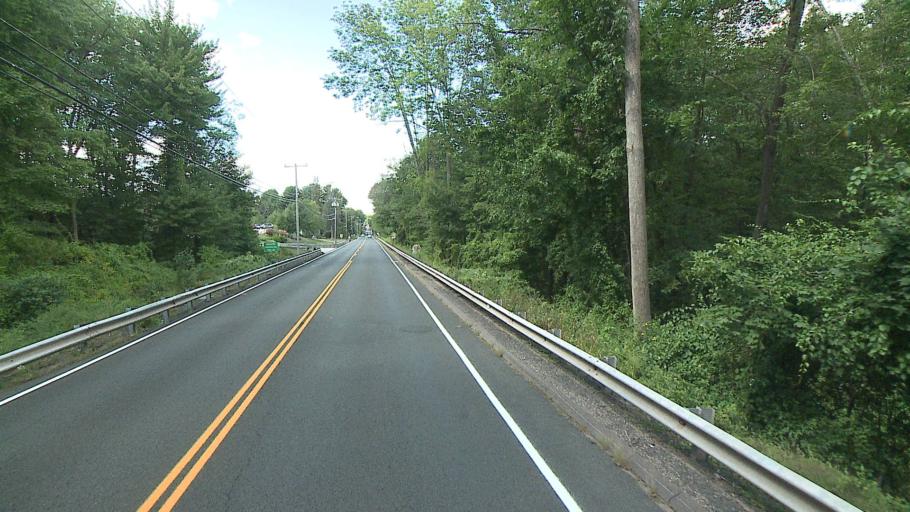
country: US
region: Connecticut
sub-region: Hartford County
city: Manchester
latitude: 41.7843
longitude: -72.4707
